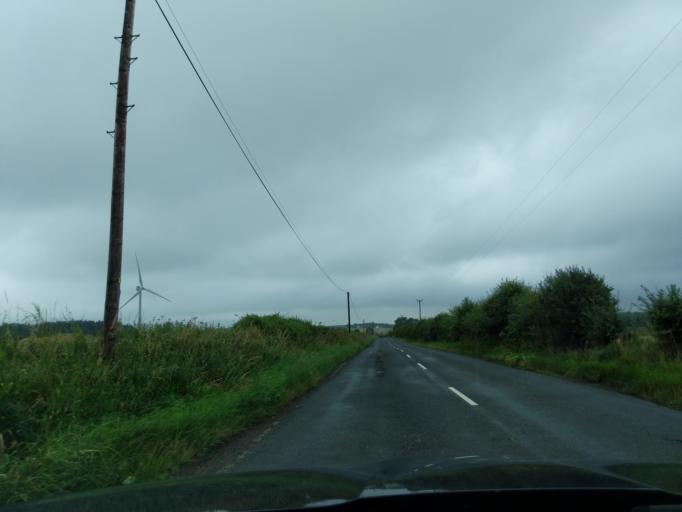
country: GB
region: England
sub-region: Northumberland
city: Ford
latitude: 55.6473
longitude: -2.0284
